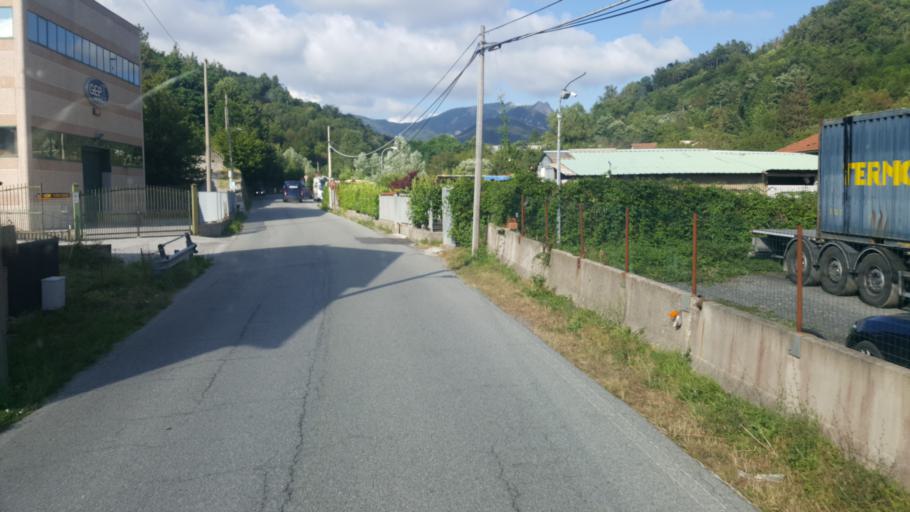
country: IT
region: Liguria
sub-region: Provincia di Genova
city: Busalla
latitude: 44.5779
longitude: 8.9677
